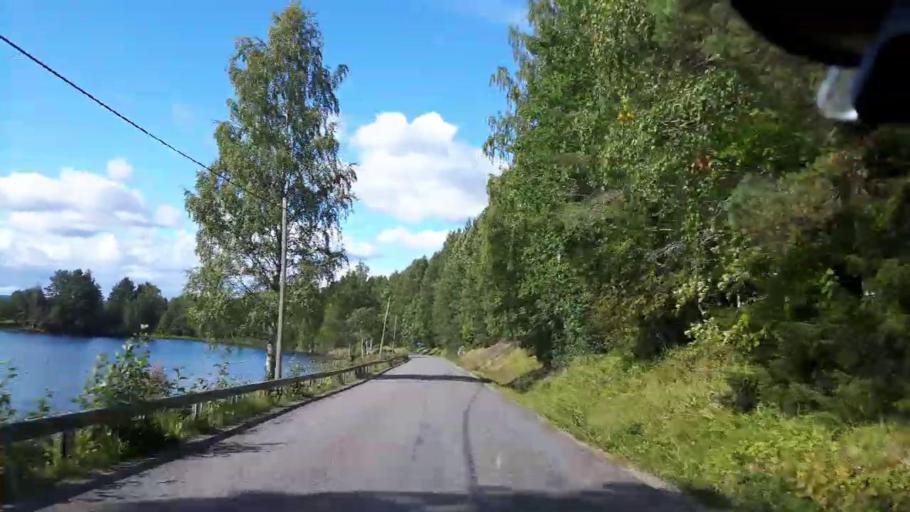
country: SE
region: Jaemtland
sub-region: Braecke Kommun
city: Braecke
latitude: 63.1760
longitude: 15.5615
